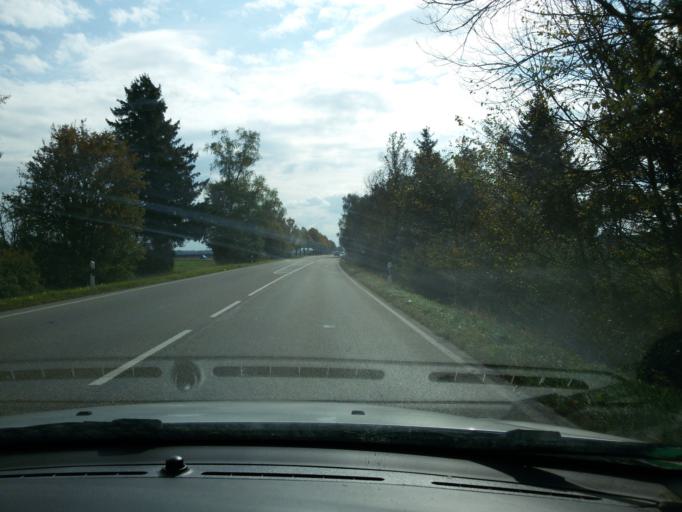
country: DE
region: Bavaria
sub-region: Upper Bavaria
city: Kaufering
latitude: 48.1125
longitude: 10.8496
